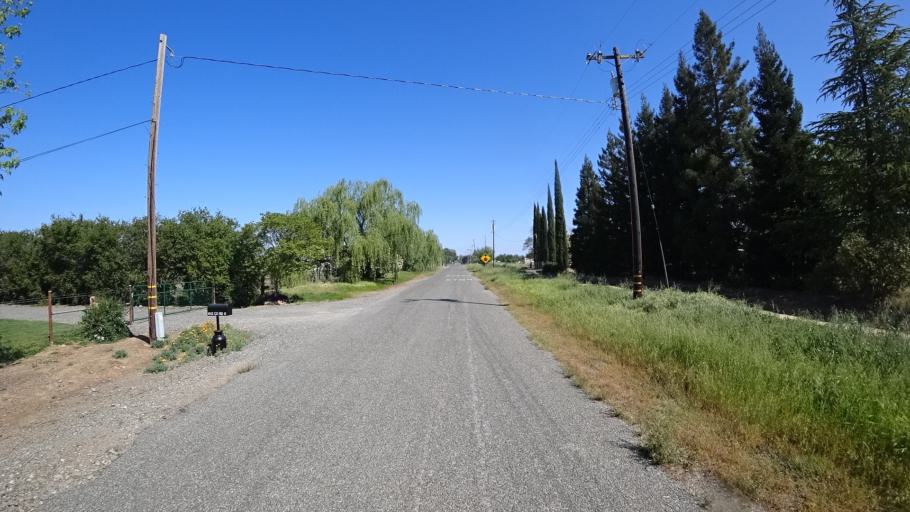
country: US
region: California
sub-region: Glenn County
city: Orland
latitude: 39.7237
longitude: -122.1924
